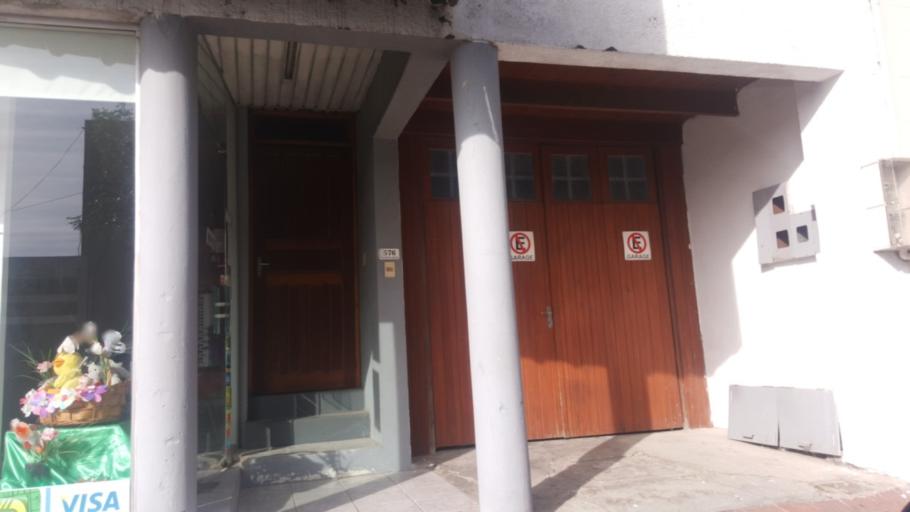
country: UY
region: Florida
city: Florida
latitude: -34.1007
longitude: -56.2159
